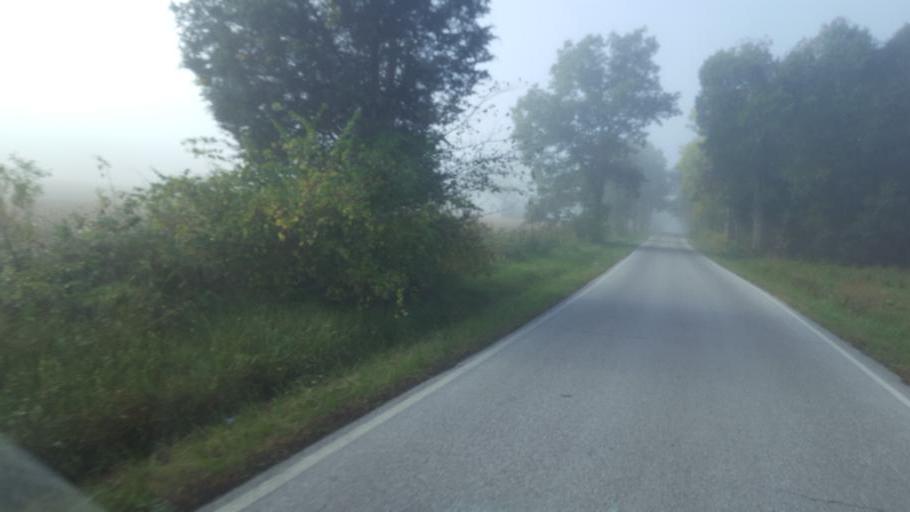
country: US
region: Kentucky
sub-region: Fleming County
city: Flemingsburg
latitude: 38.4831
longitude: -83.5996
